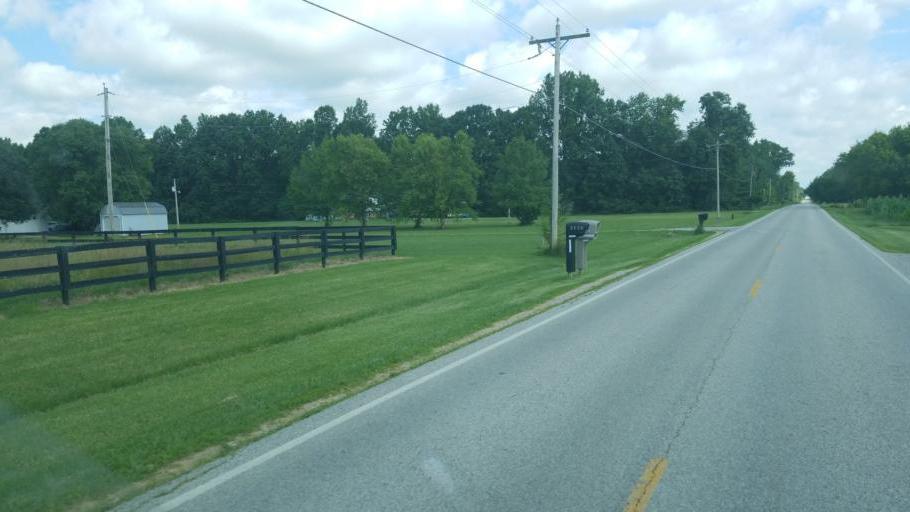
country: US
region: Ohio
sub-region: Delaware County
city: Sunbury
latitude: 40.3005
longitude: -82.9343
